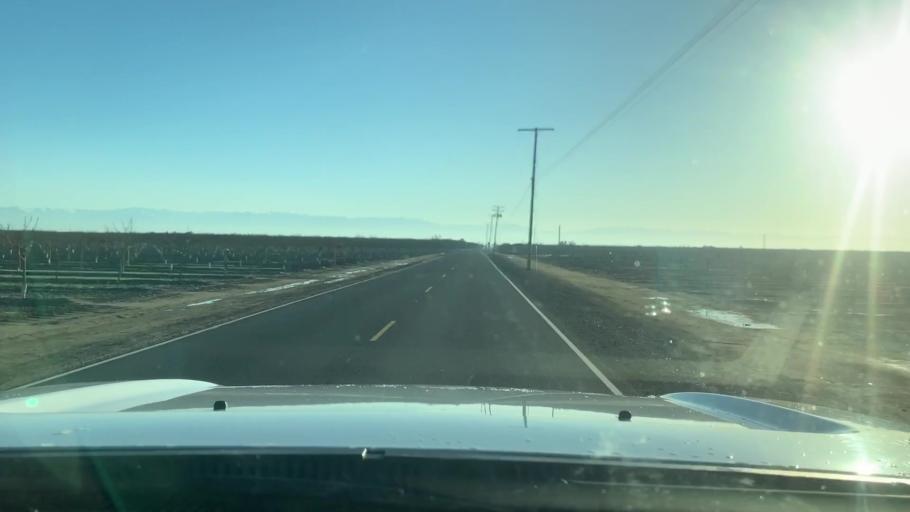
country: US
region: California
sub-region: Tulare County
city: Tulare
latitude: 36.2031
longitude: -119.4609
